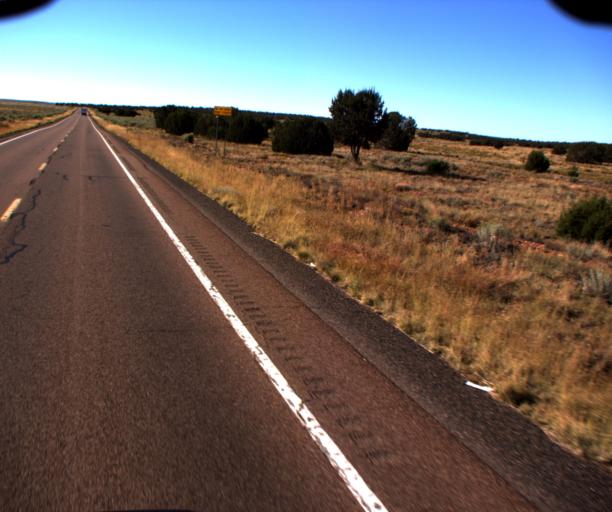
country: US
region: Arizona
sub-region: Navajo County
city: Heber-Overgaard
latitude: 34.5678
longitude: -110.4139
